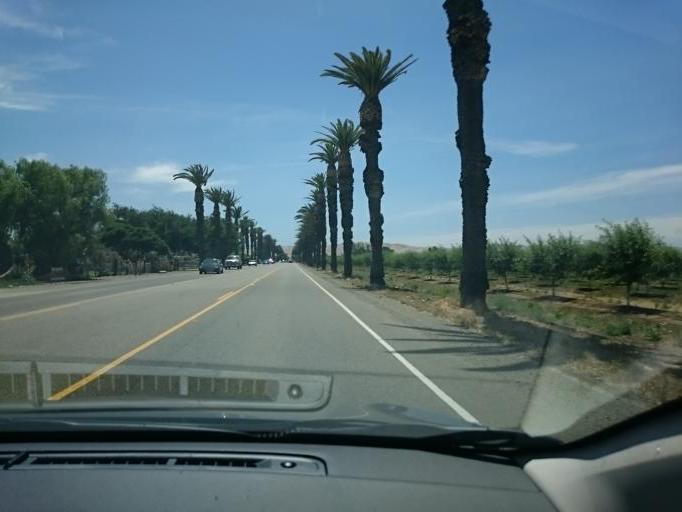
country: US
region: California
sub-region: Stanislaus County
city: Patterson
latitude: 37.4888
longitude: -121.0923
